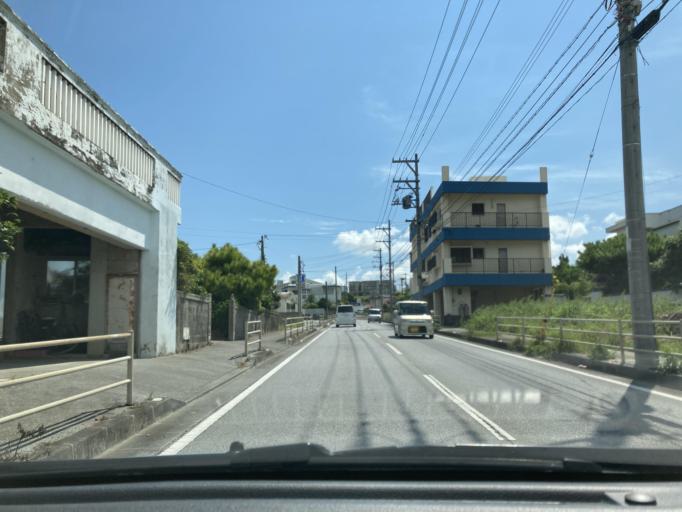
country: JP
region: Okinawa
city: Tomigusuku
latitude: 26.1813
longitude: 127.7411
